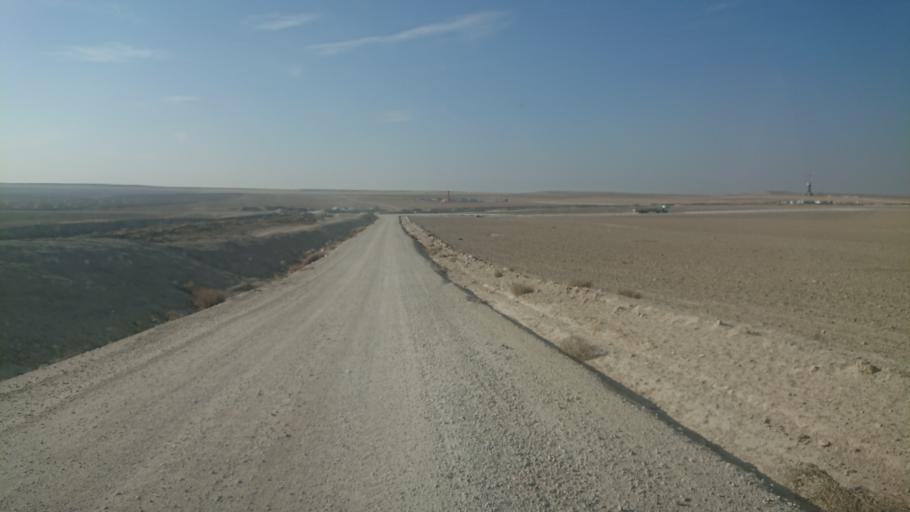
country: TR
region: Aksaray
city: Sultanhani
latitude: 38.0677
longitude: 33.6193
